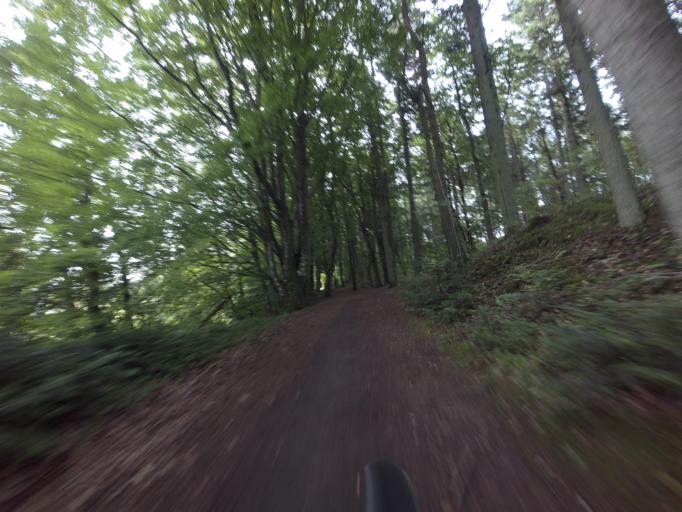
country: DK
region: North Denmark
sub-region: Hjorring Kommune
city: Sindal
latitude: 57.5845
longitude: 10.1805
